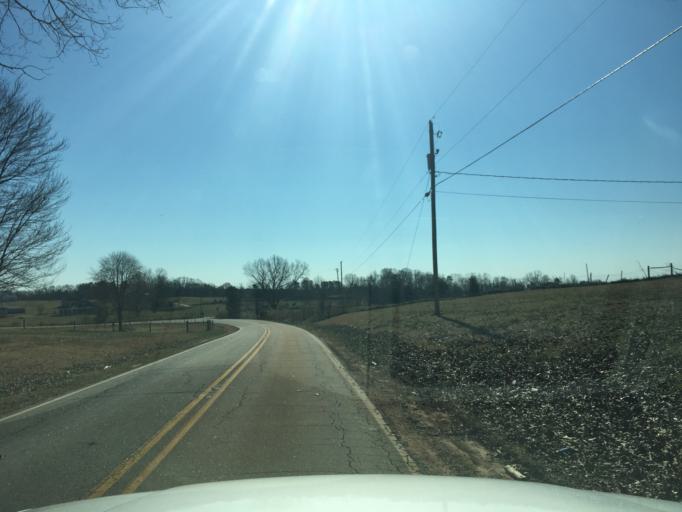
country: US
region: South Carolina
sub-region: Pickens County
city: Liberty
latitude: 34.8215
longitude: -82.7807
